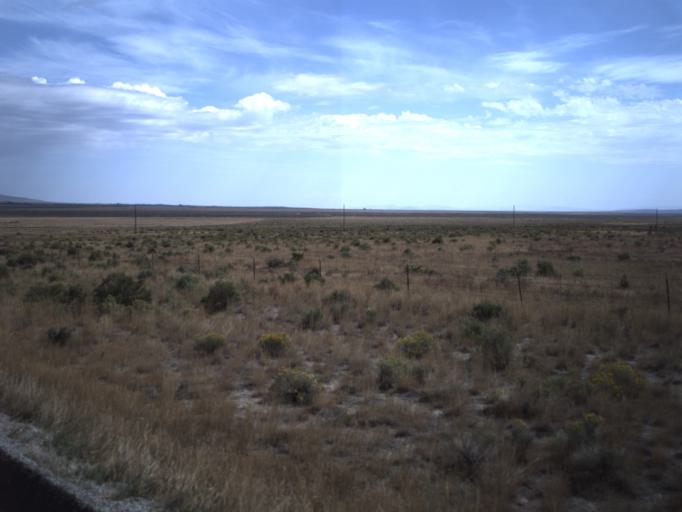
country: US
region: Idaho
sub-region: Cassia County
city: Burley
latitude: 41.7692
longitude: -113.5034
